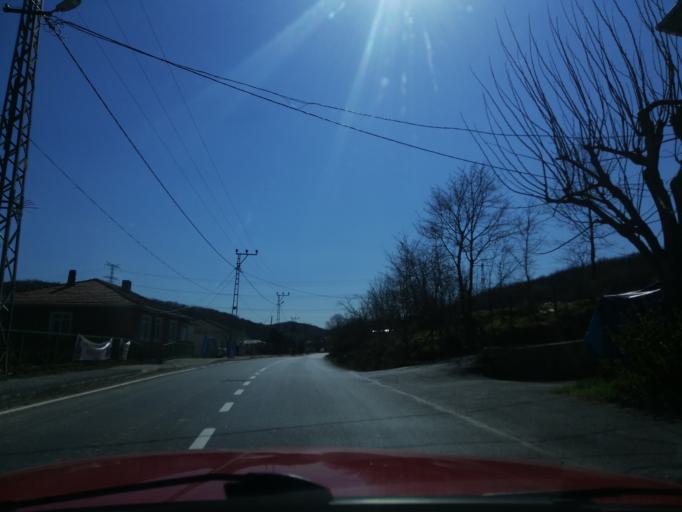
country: TR
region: Istanbul
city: Mahmut Sevket Pasa
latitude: 41.1321
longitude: 29.1633
